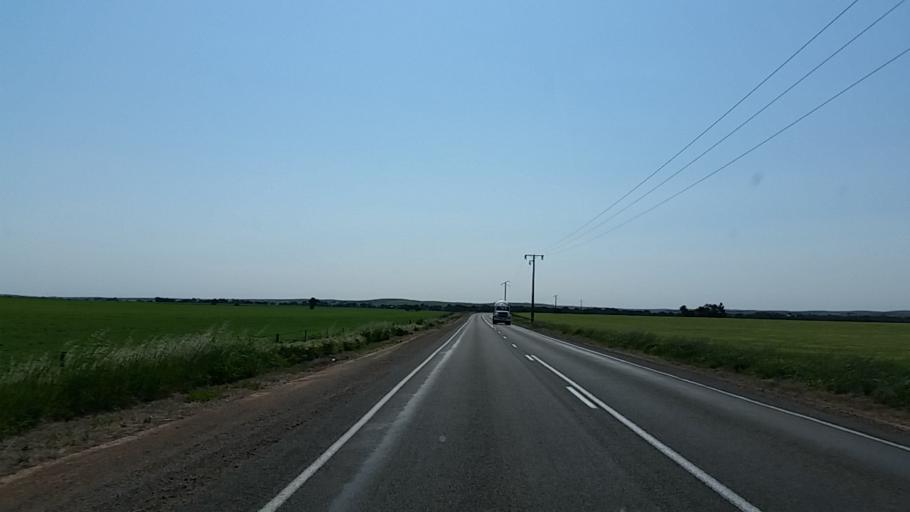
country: AU
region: South Australia
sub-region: Port Pirie City and Dists
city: Crystal Brook
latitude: -33.2734
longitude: 138.3135
